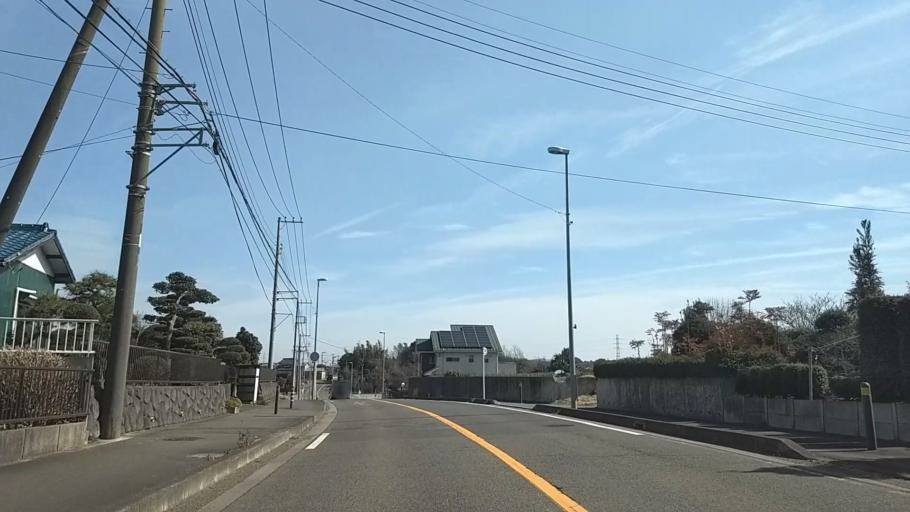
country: JP
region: Kanagawa
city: Chigasaki
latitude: 35.3876
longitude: 139.4077
